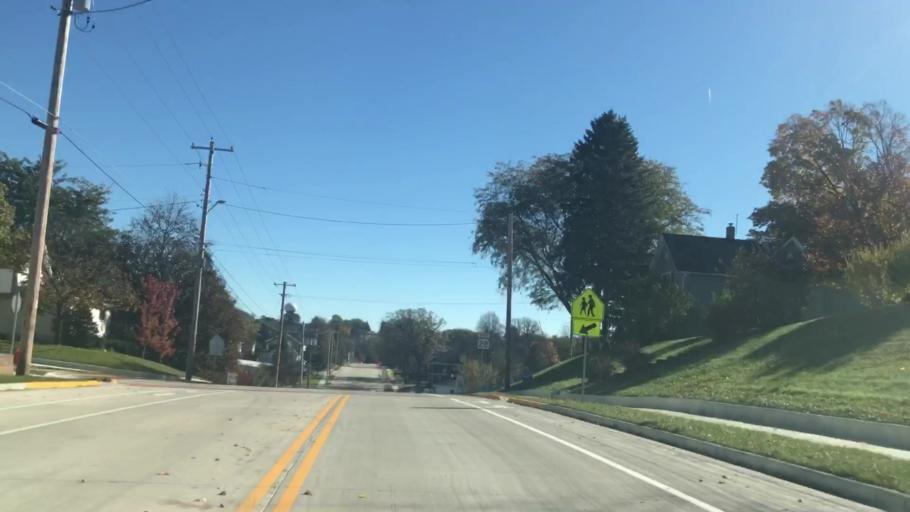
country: US
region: Wisconsin
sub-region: Dodge County
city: Mayville
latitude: 43.4940
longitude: -88.5529
